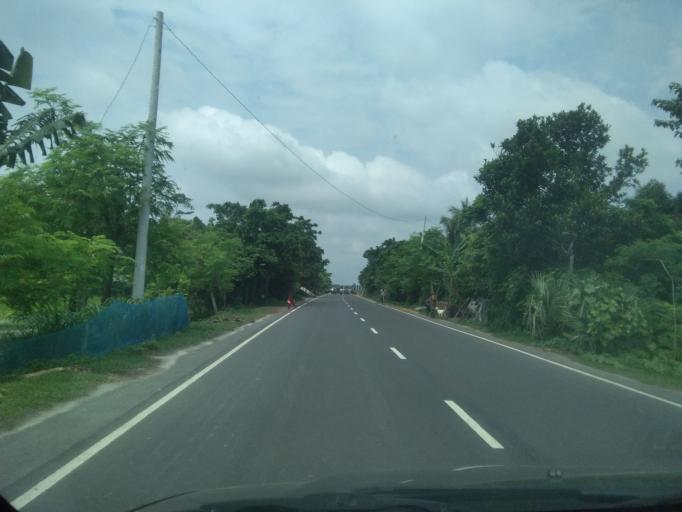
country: BD
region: Khulna
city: Kesabpur
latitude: 22.7896
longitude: 89.2182
